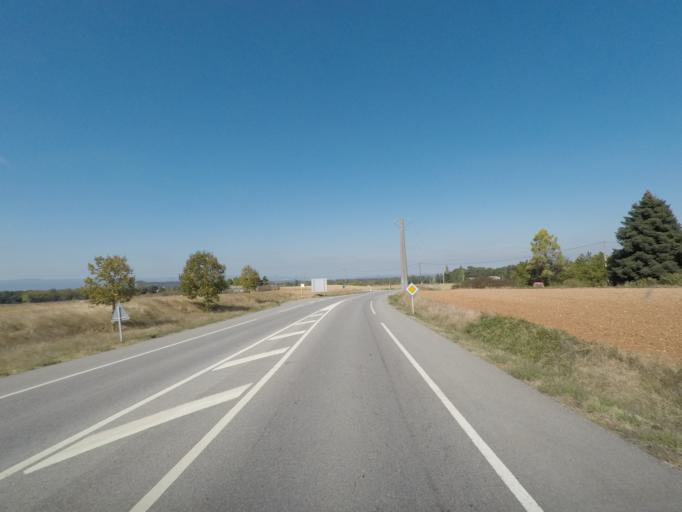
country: FR
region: Rhone-Alpes
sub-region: Departement de la Drome
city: Upie
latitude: 44.8206
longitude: 5.0106
